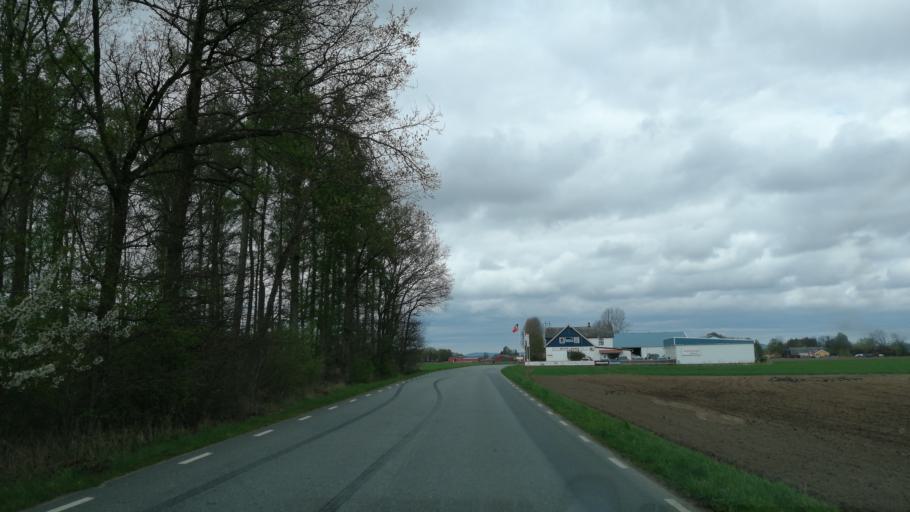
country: SE
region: Skane
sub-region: Kristianstads Kommun
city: Fjalkinge
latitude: 56.0561
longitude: 14.3329
